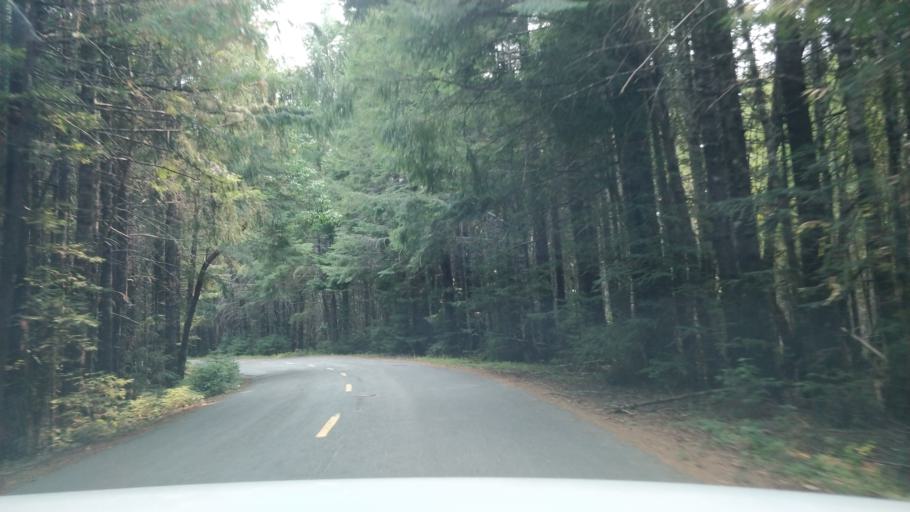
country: US
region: California
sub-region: Humboldt County
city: Westhaven-Moonstone
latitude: 41.2399
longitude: -123.9824
